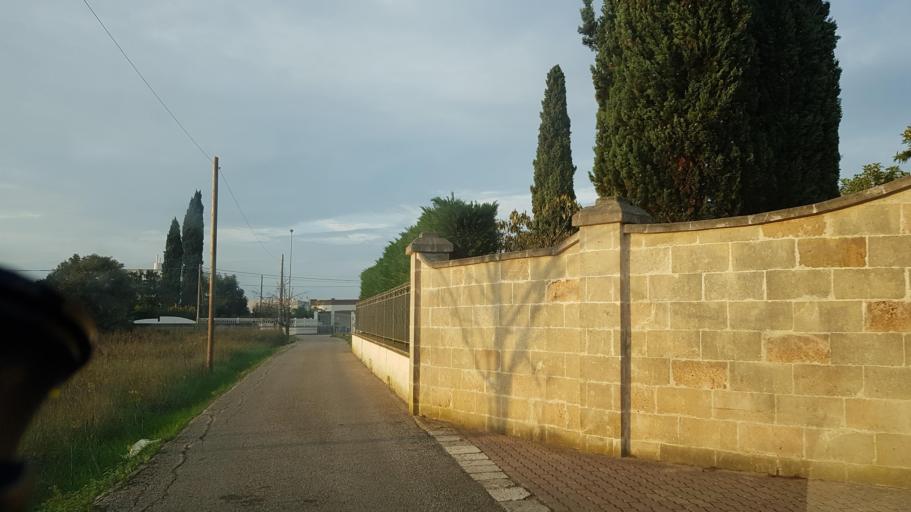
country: IT
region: Apulia
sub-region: Provincia di Brindisi
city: Latiano
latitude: 40.5568
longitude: 17.7310
